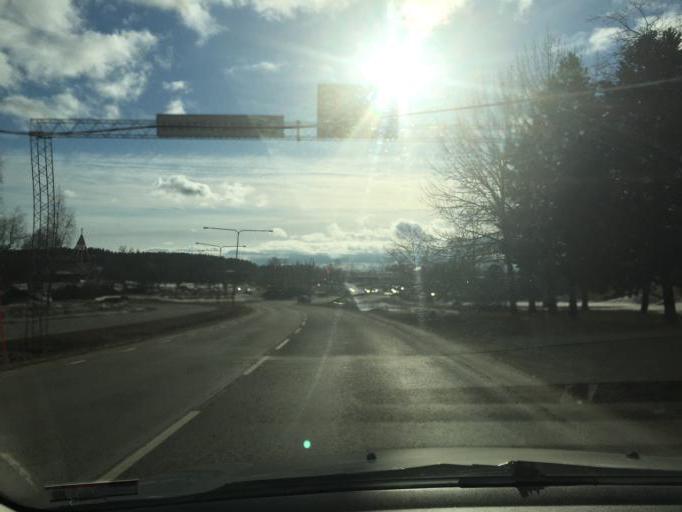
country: SE
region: Norrbotten
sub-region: Lulea Kommun
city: Lulea
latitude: 65.5810
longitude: 22.1959
